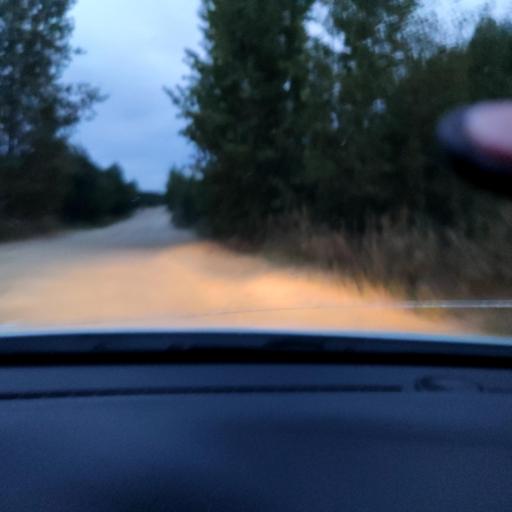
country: RU
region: Mariy-El
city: Volzhsk
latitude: 55.8841
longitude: 48.3903
